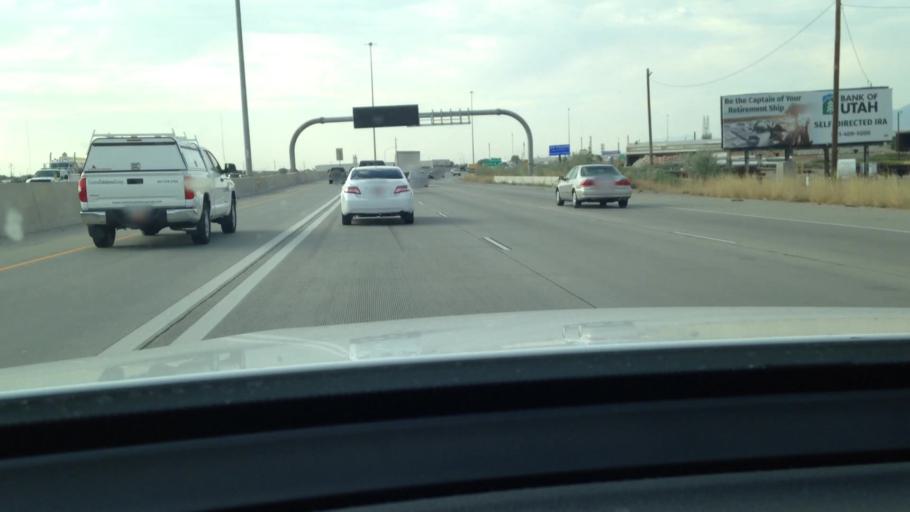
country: US
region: Utah
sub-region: Davis County
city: North Salt Lake
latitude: 40.8061
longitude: -111.9226
